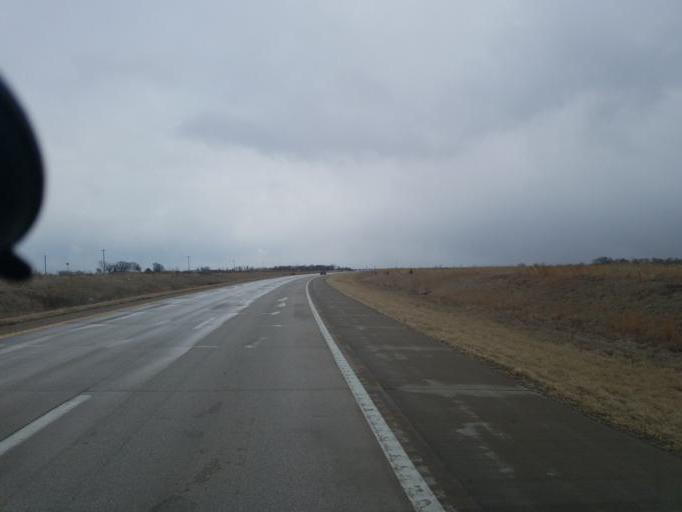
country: US
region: Missouri
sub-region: Randolph County
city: Moberly
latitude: 39.4898
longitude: -92.4347
